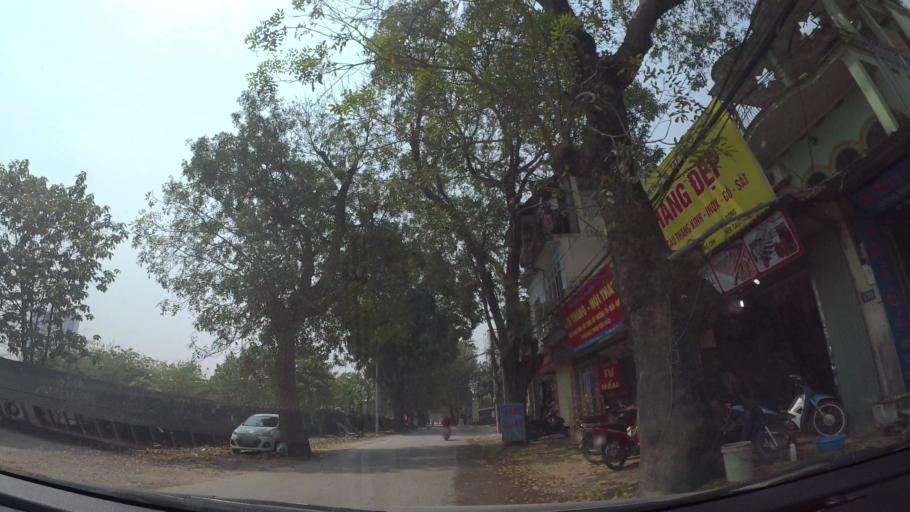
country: VN
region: Ha Noi
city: Ha Dong
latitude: 20.9919
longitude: 105.7626
